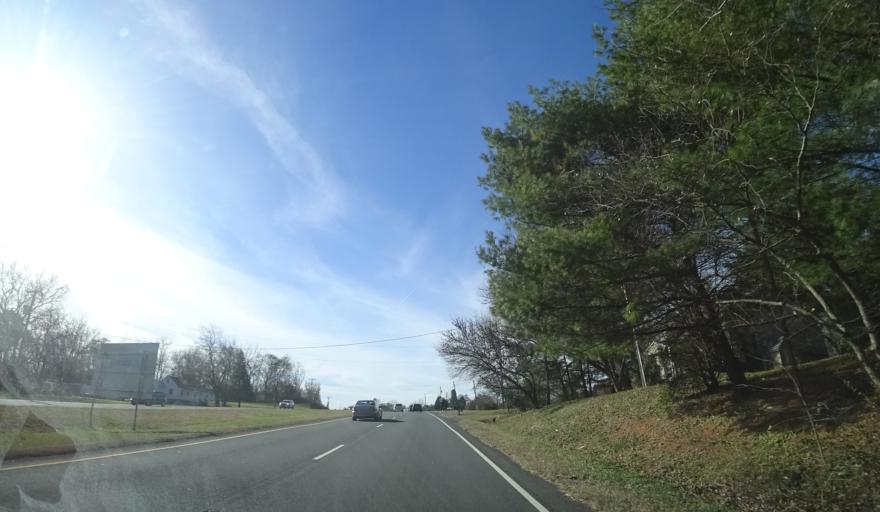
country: US
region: Virginia
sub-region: Prince William County
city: Haymarket
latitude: 38.7803
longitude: -77.6747
